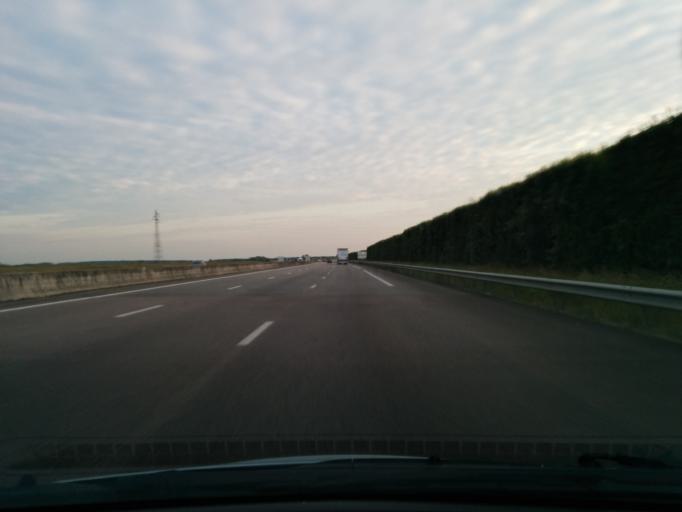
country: FR
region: Haute-Normandie
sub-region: Departement de l'Eure
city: Saint-Aubin-sur-Gaillon
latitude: 49.1242
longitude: 1.3263
